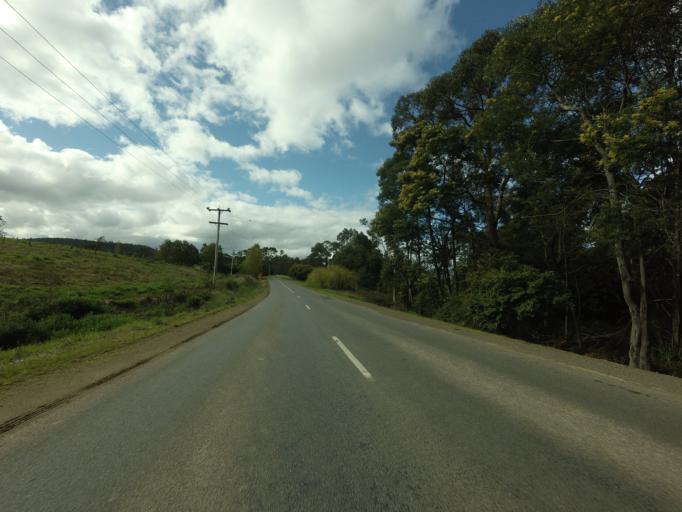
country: AU
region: Tasmania
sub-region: Huon Valley
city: Geeveston
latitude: -43.1925
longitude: 146.9587
